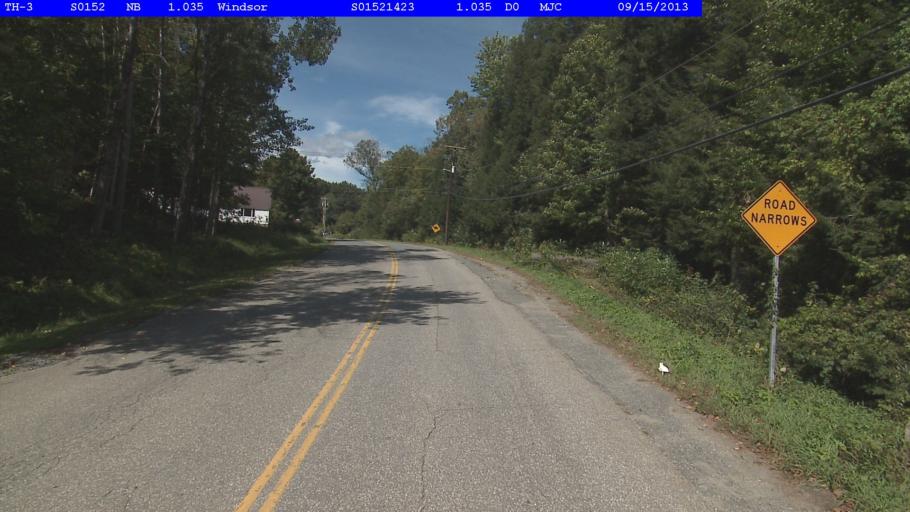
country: US
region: Vermont
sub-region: Windsor County
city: Windsor
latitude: 43.4880
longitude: -72.4012
